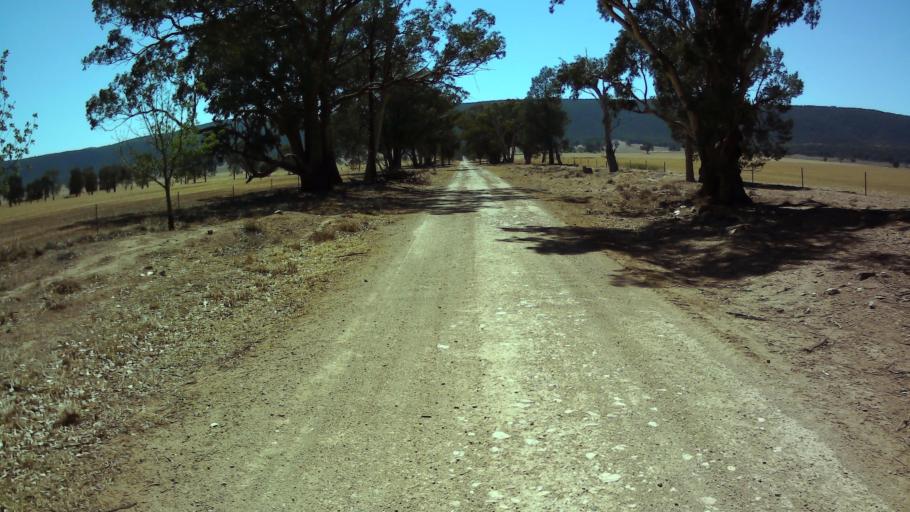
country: AU
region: New South Wales
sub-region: Weddin
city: Grenfell
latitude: -33.7019
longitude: 148.3226
